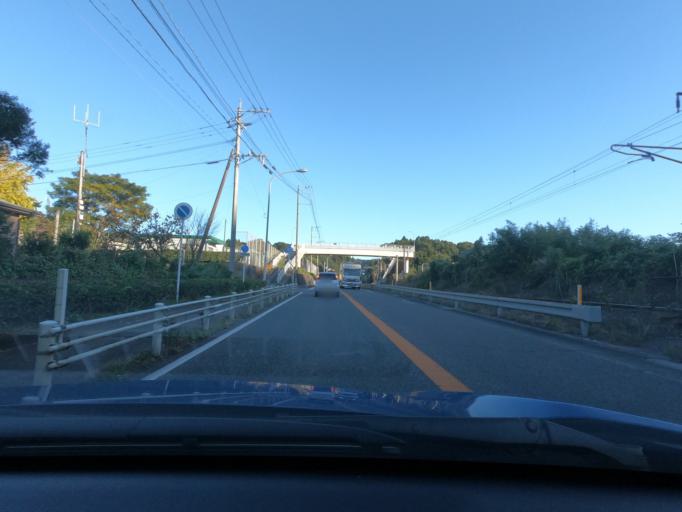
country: JP
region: Kagoshima
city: Satsumasendai
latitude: 31.8499
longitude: 130.2426
